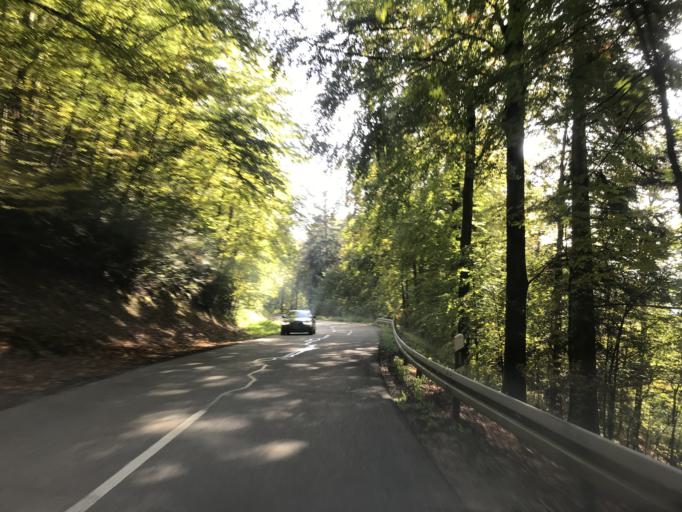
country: DE
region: Baden-Wuerttemberg
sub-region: Freiburg Region
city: Wehr
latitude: 47.6383
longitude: 7.9311
